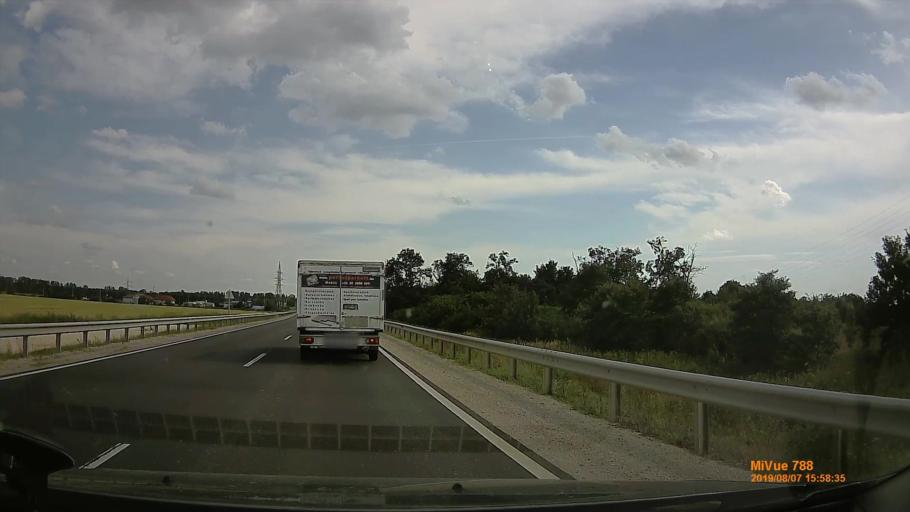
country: HU
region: Vas
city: Kormend
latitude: 47.0250
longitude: 16.6137
